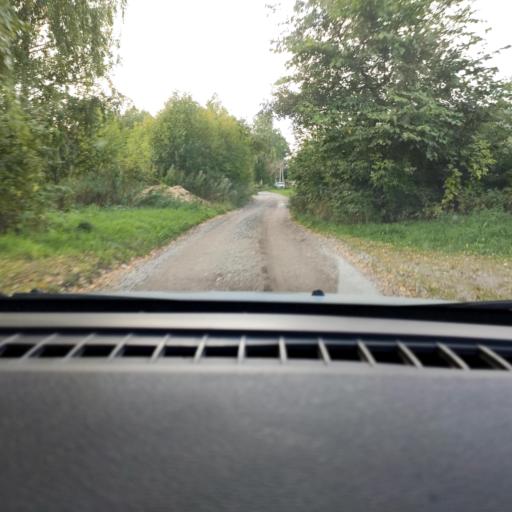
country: RU
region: Perm
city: Perm
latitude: 58.0981
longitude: 56.3735
